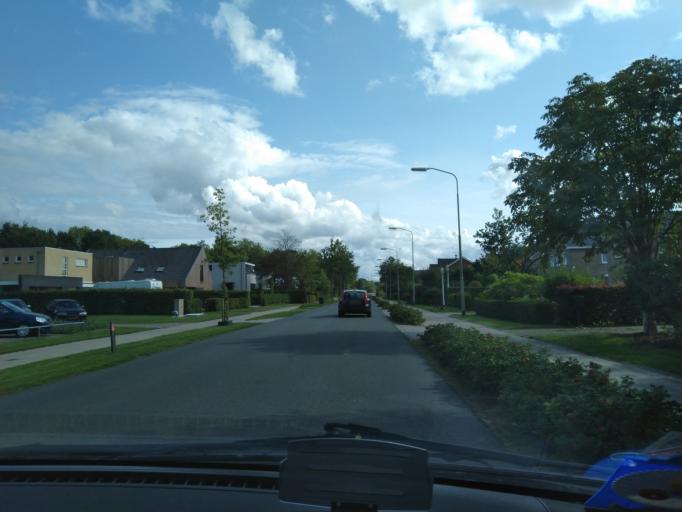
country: NL
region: Groningen
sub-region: Gemeente Groningen
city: Groningen
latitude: 53.1755
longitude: 6.5449
